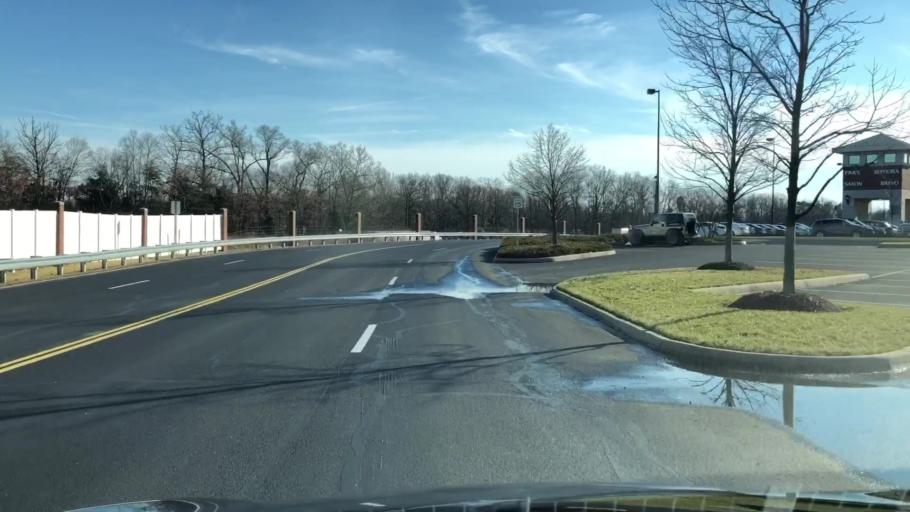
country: US
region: Virginia
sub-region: City of Fredericksburg
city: Fredericksburg
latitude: 38.2918
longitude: -77.5087
